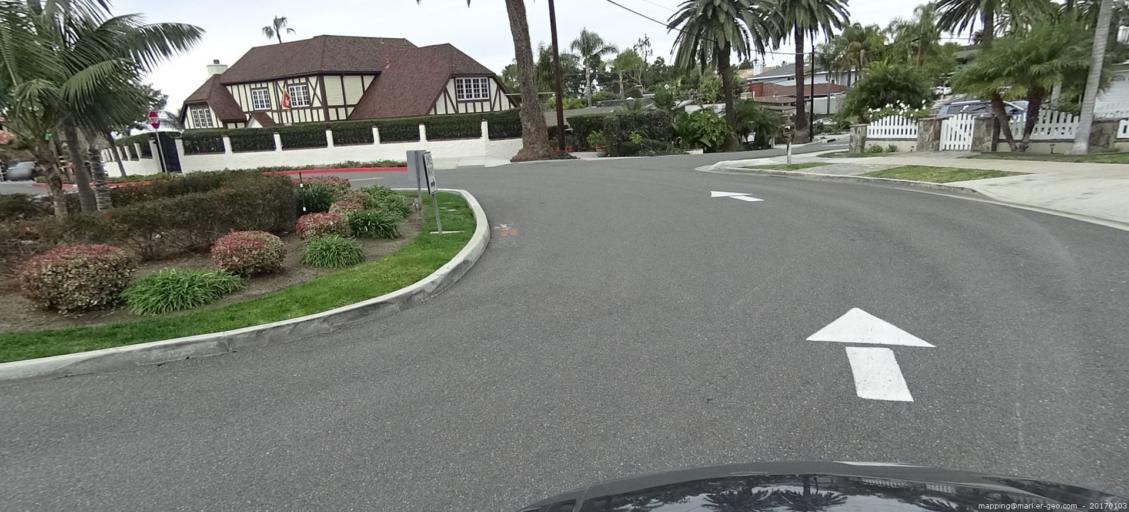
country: US
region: California
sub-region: Orange County
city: Dana Point
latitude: 33.4542
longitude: -117.6626
